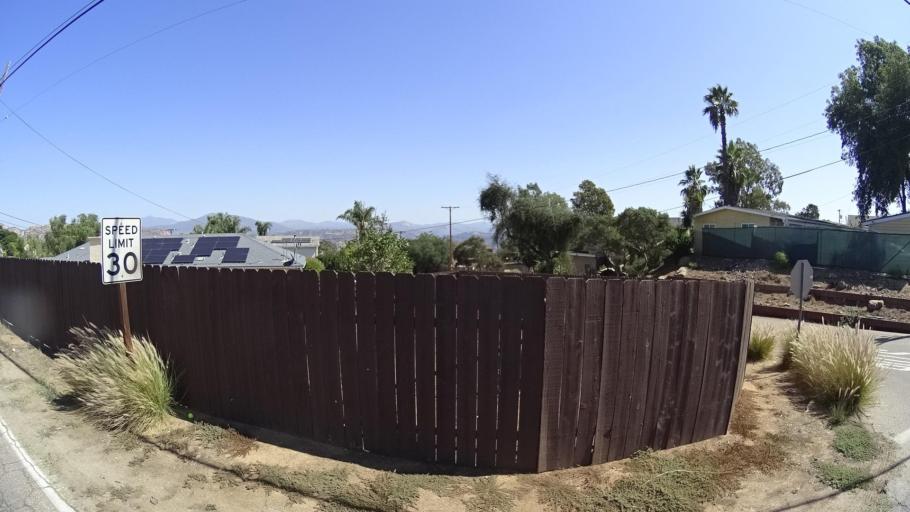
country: US
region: California
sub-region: San Diego County
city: Crest
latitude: 32.8114
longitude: -116.8636
